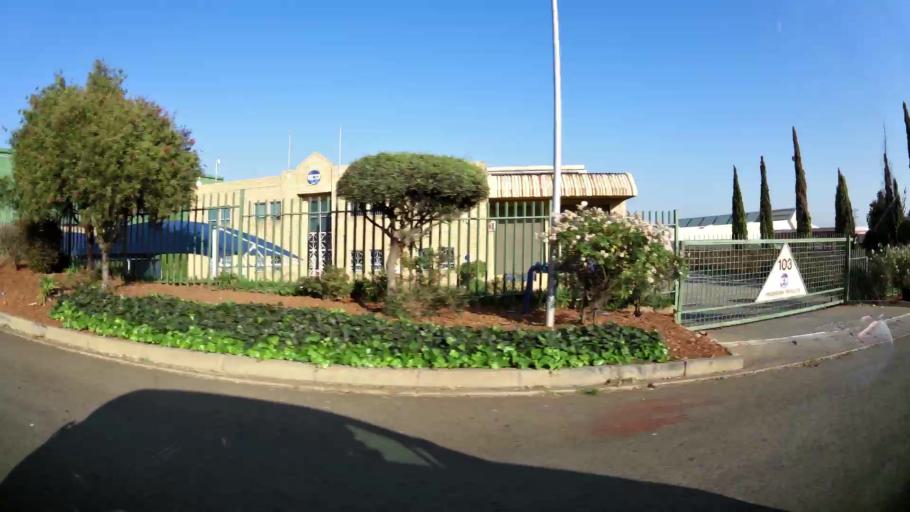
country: ZA
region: Gauteng
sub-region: City of Johannesburg Metropolitan Municipality
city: Modderfontein
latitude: -26.1512
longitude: 28.1842
